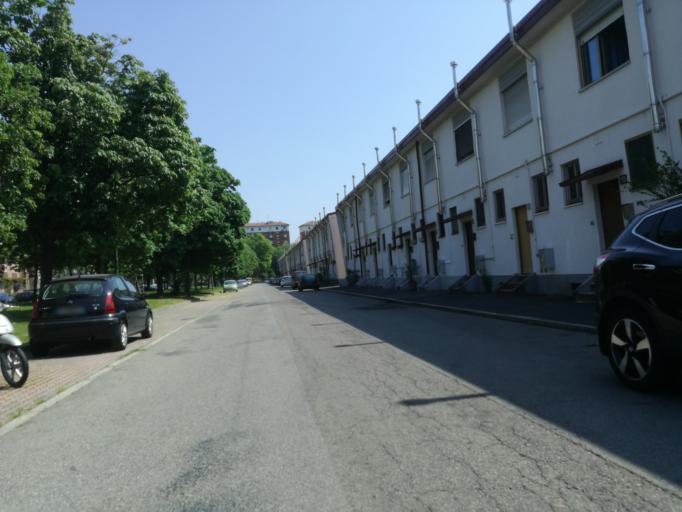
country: IT
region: Lombardy
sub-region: Citta metropolitana di Milano
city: Romano Banco
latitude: 45.4526
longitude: 9.1300
